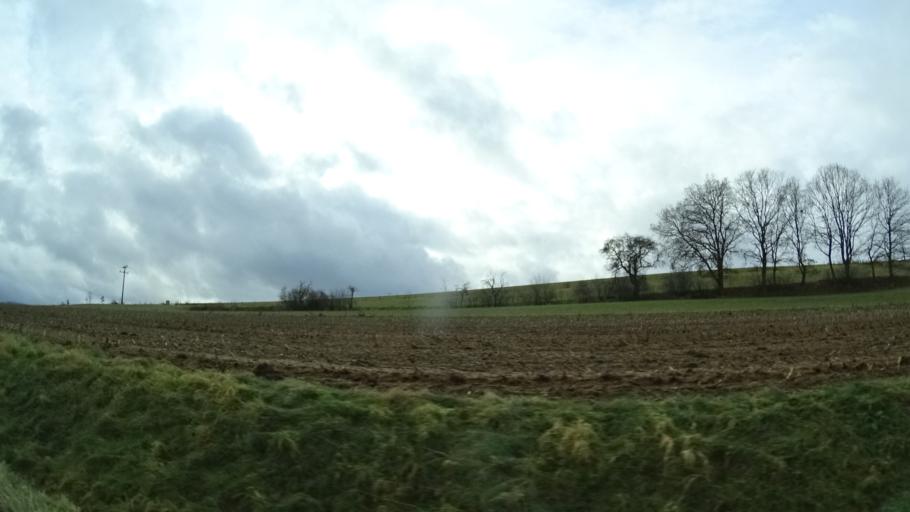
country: DE
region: Hesse
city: Tann
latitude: 50.6195
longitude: 10.0280
